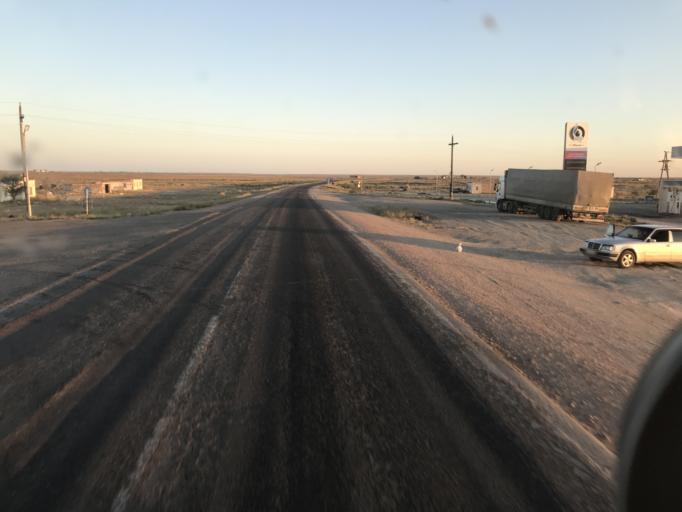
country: KZ
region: Qaraghandy
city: Saryshaghan
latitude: 46.0198
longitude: 73.5916
